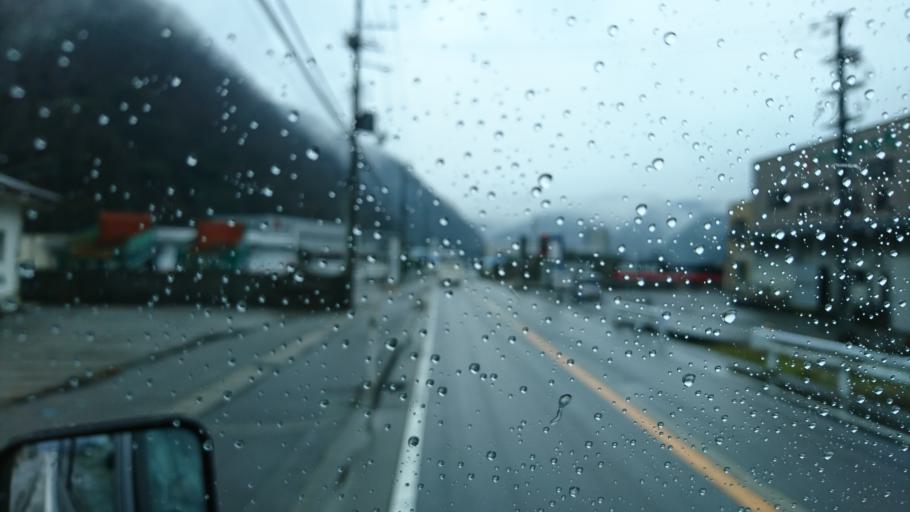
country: JP
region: Tottori
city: Tottori
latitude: 35.5808
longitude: 134.4895
